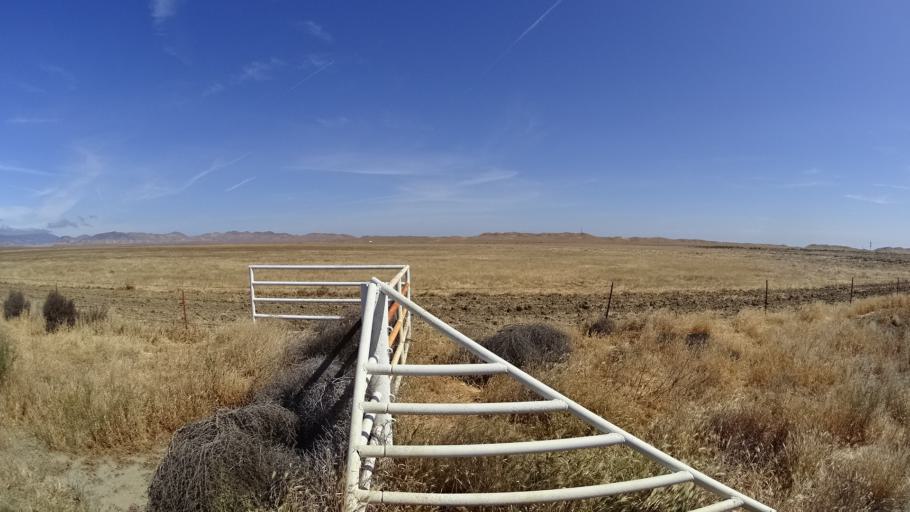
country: US
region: California
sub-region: Kings County
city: Avenal
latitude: 35.8179
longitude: -120.0852
